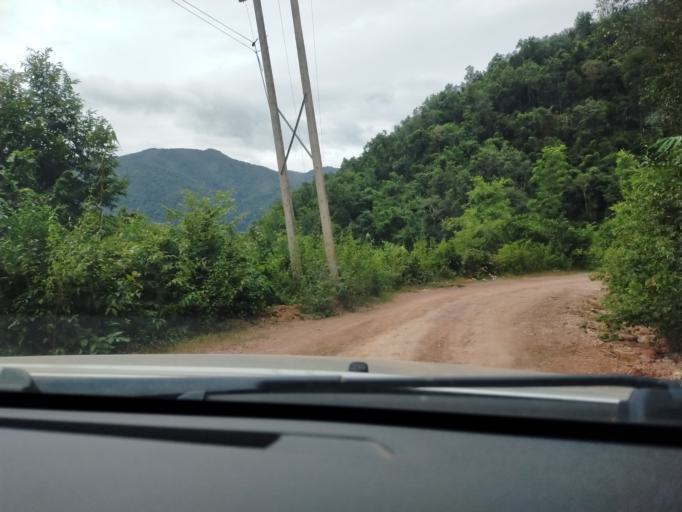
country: TH
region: Nan
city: Chaloem Phra Kiat
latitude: 19.8039
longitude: 101.3617
